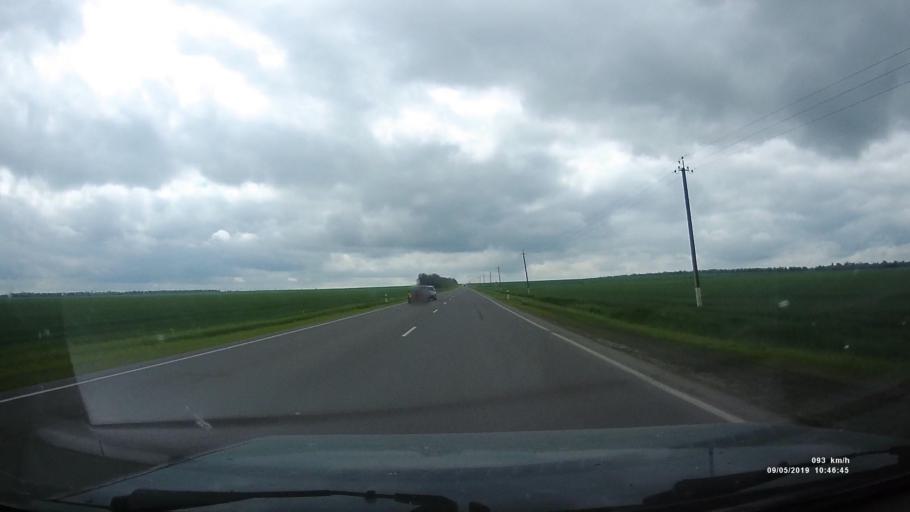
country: RU
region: Rostov
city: Peshkovo
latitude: 46.9805
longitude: 39.3558
